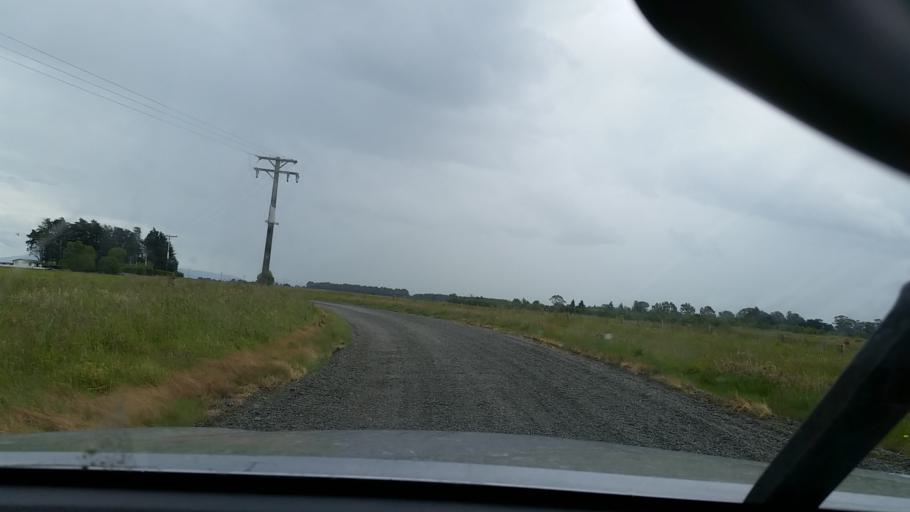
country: NZ
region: Southland
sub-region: Southland District
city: Winton
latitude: -46.0069
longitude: 168.1967
